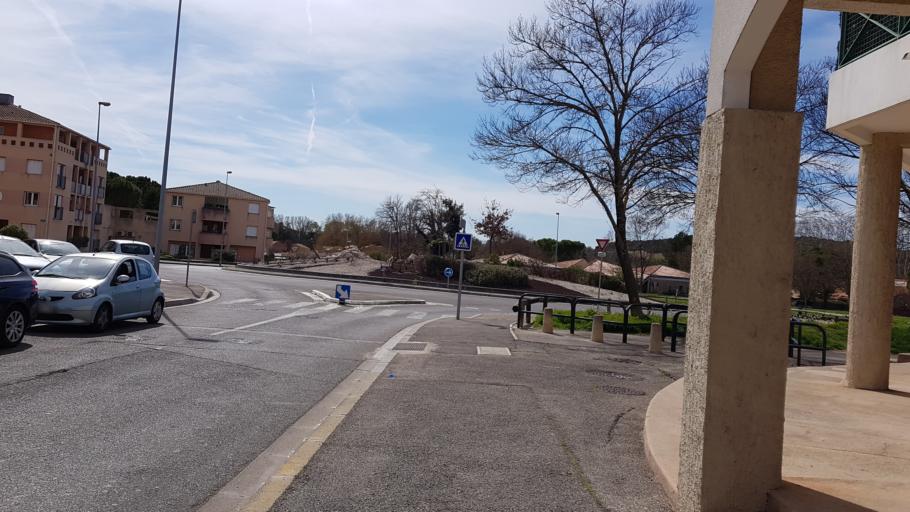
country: FR
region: Provence-Alpes-Cote d'Azur
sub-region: Departement des Bouches-du-Rhone
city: Bouc-Bel-Air
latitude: 43.4870
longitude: 5.4168
